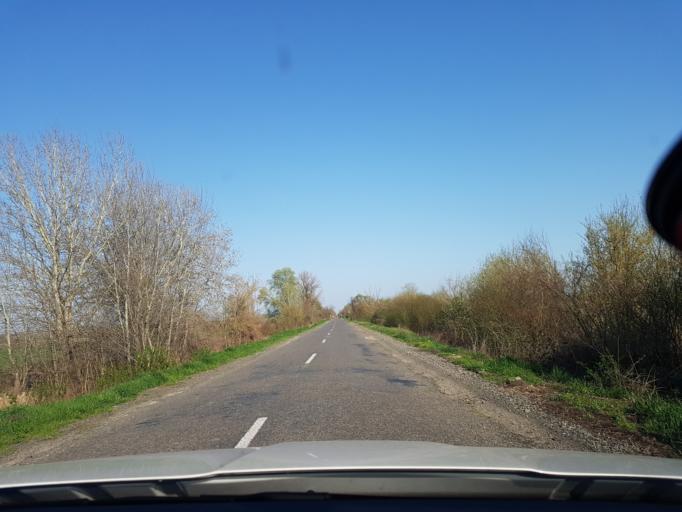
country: HU
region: Tolna
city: Bogyiszlo
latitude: 46.3332
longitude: 18.8143
